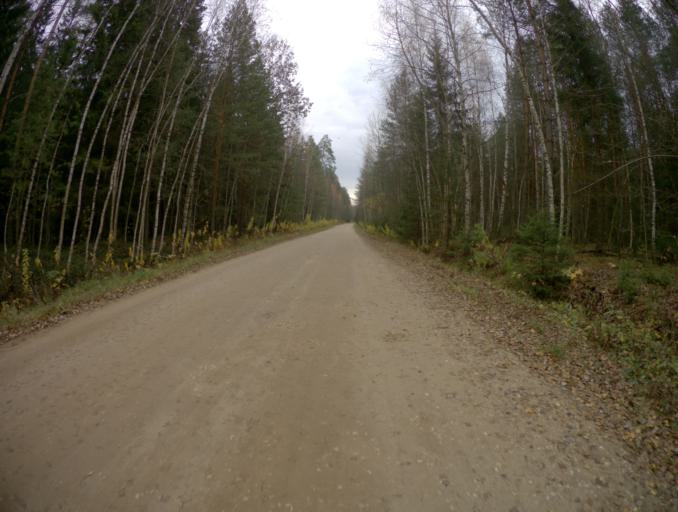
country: RU
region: Moskovskaya
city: Malaya Dubna
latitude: 55.9266
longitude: 38.9619
